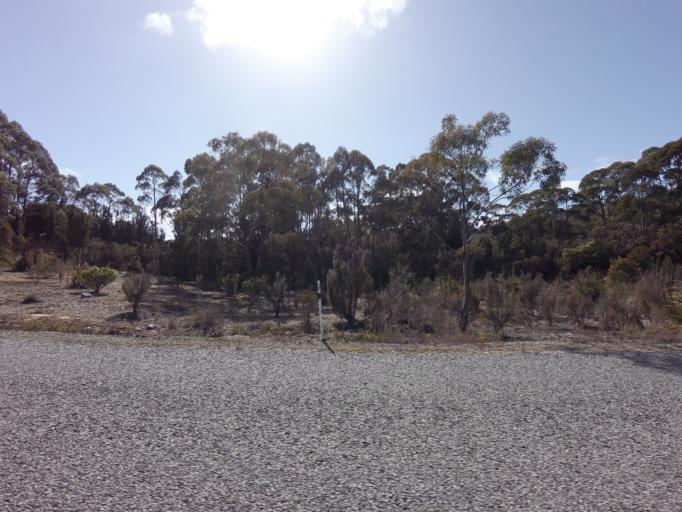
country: AU
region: Tasmania
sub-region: Huon Valley
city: Geeveston
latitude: -42.7722
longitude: 146.3973
